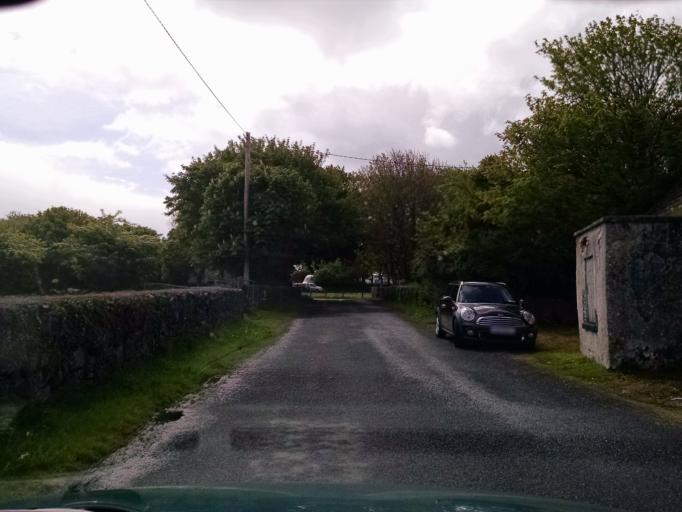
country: IE
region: Connaught
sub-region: County Galway
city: Bearna
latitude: 53.1560
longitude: -9.0846
